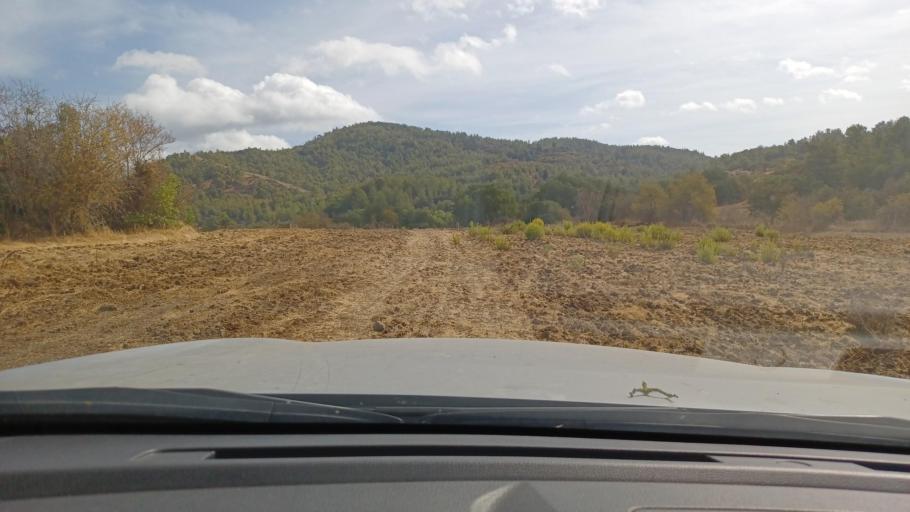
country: CY
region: Pafos
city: Polis
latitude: 35.0095
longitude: 32.5121
